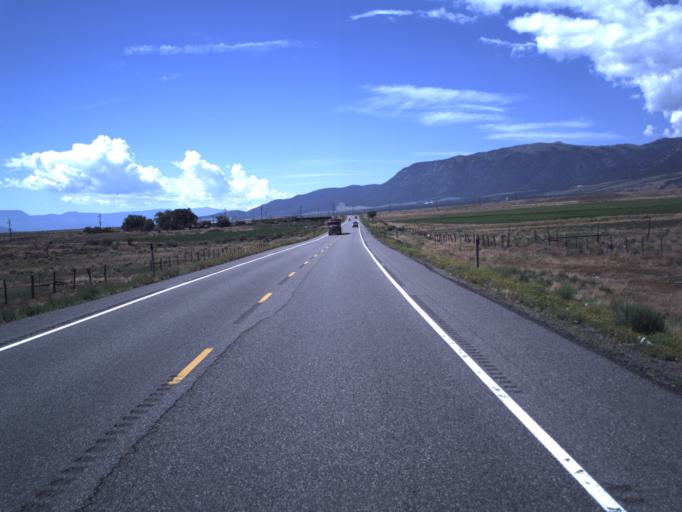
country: US
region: Utah
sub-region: Piute County
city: Junction
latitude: 38.4390
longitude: -112.2302
